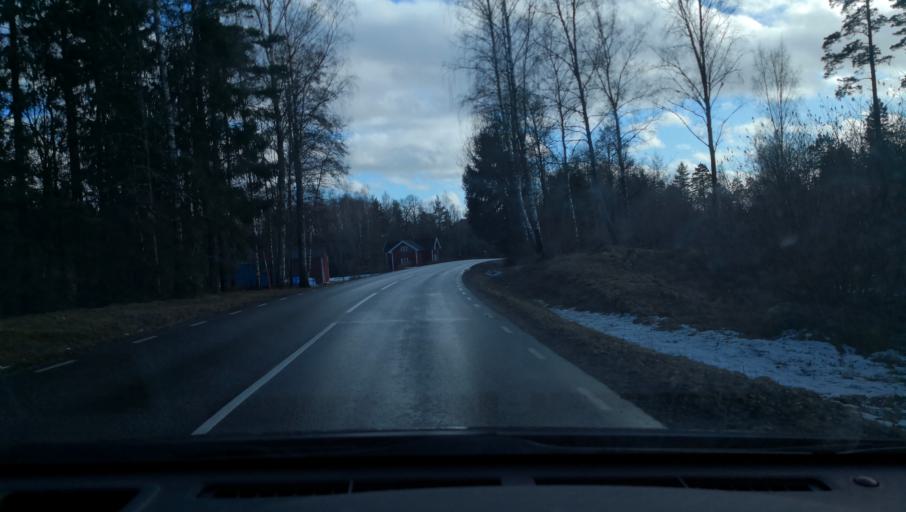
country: SE
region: Vaestmanland
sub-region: Arboga Kommun
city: Arboga
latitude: 59.3601
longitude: 15.8487
